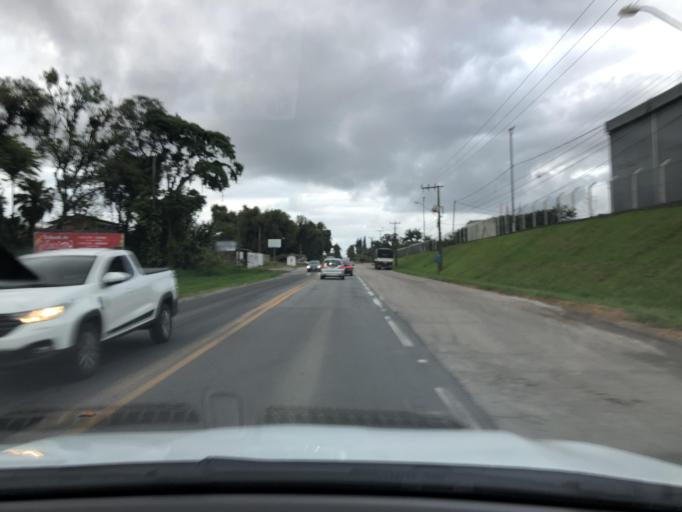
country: BR
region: Santa Catarina
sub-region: Sao Francisco Do Sul
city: Sao Francisco do Sul
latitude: -26.2882
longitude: -48.6459
